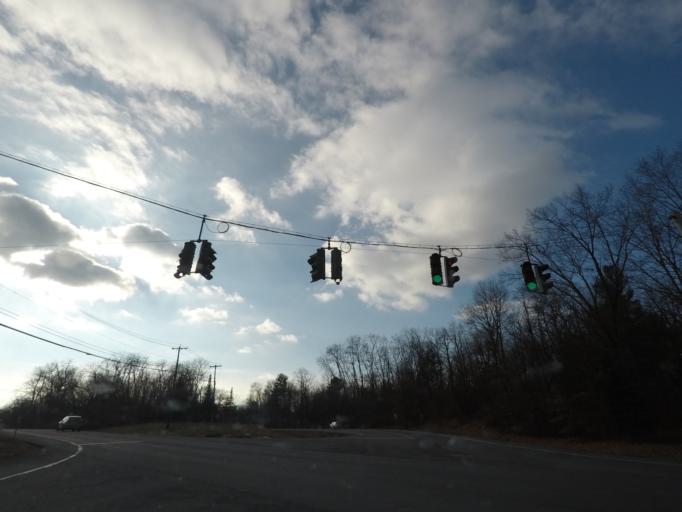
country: US
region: New York
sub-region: Albany County
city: Voorheesville
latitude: 42.6585
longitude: -73.9157
